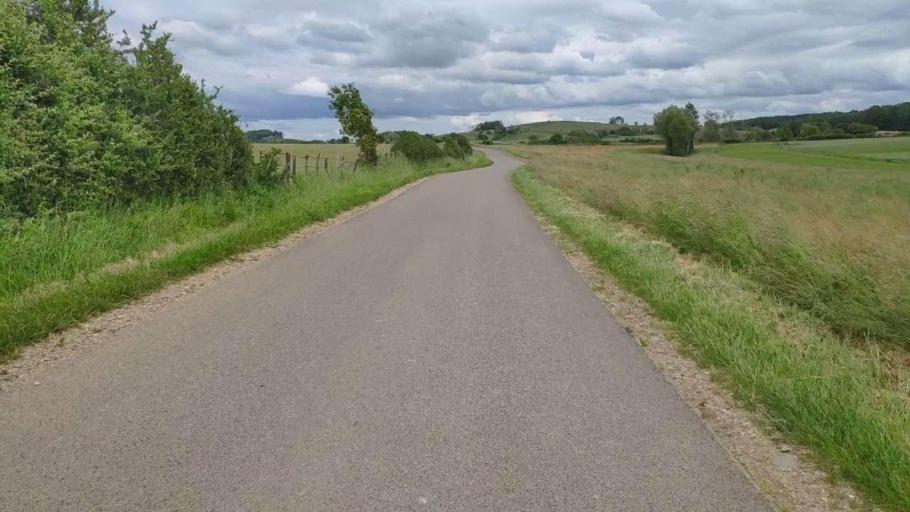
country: FR
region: Franche-Comte
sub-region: Departement du Jura
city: Bletterans
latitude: 46.7417
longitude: 5.5072
